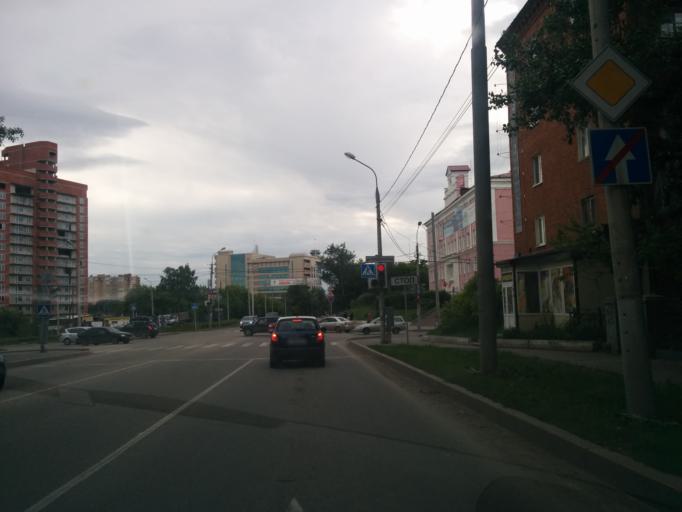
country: RU
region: Perm
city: Perm
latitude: 58.0032
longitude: 56.2083
